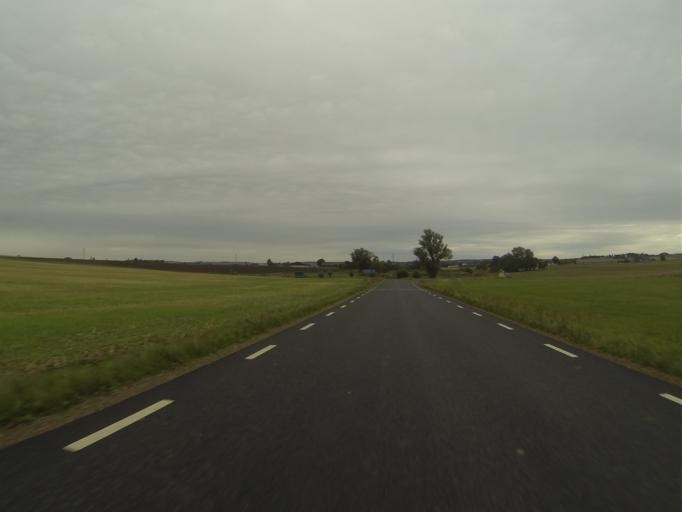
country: SE
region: Skane
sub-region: Lunds Kommun
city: Genarp
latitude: 55.6226
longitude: 13.3307
